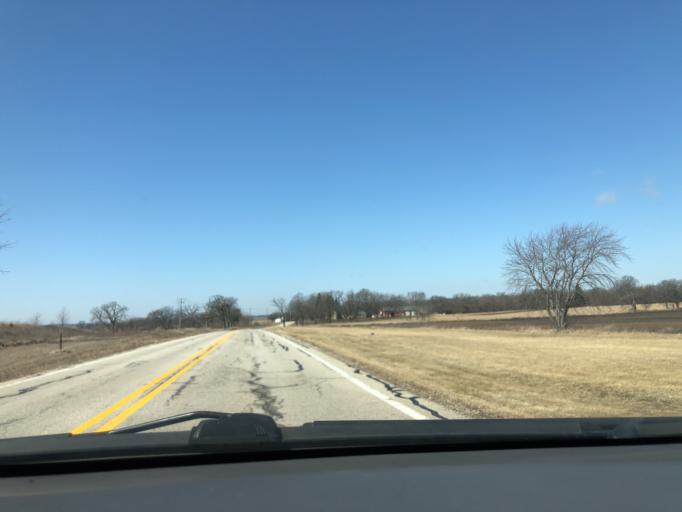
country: US
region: Illinois
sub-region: Kane County
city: Hampshire
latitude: 42.1276
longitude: -88.5175
